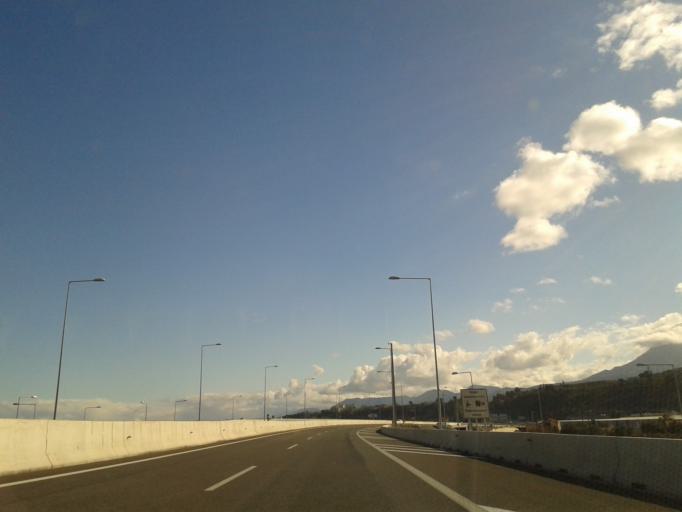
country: GR
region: West Greece
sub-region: Nomos Achaias
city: Aigio
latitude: 38.2646
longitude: 22.0566
